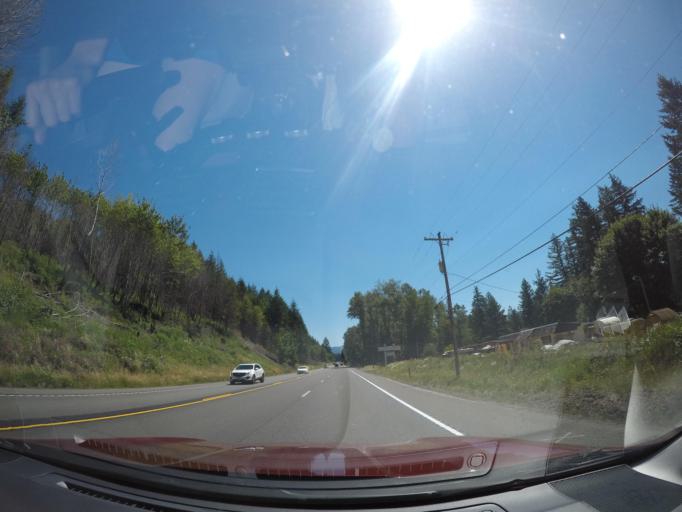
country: US
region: Oregon
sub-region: Linn County
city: Mill City
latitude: 44.7564
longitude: -122.4539
